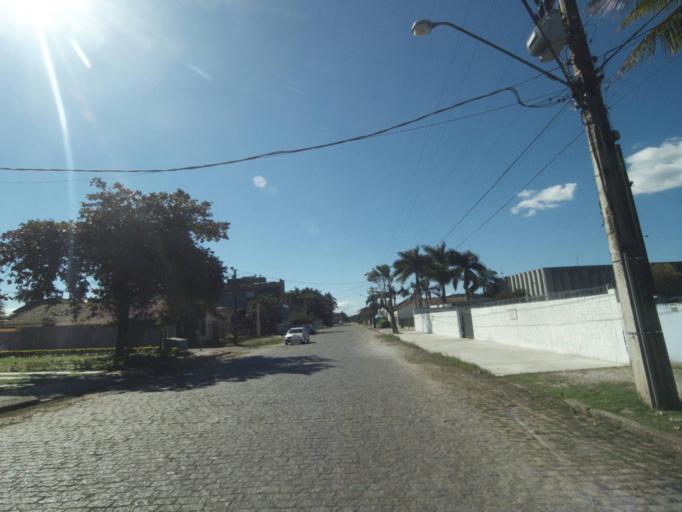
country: BR
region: Parana
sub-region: Paranagua
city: Paranagua
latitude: -25.5160
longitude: -48.5010
